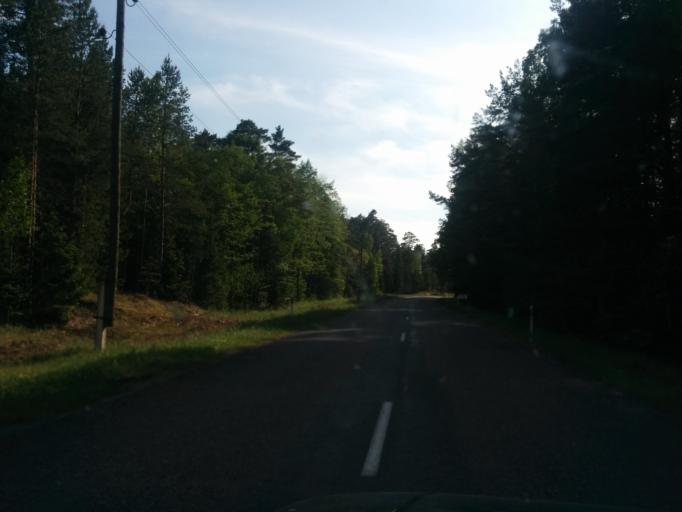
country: LV
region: Dundaga
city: Dundaga
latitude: 57.6707
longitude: 22.3204
